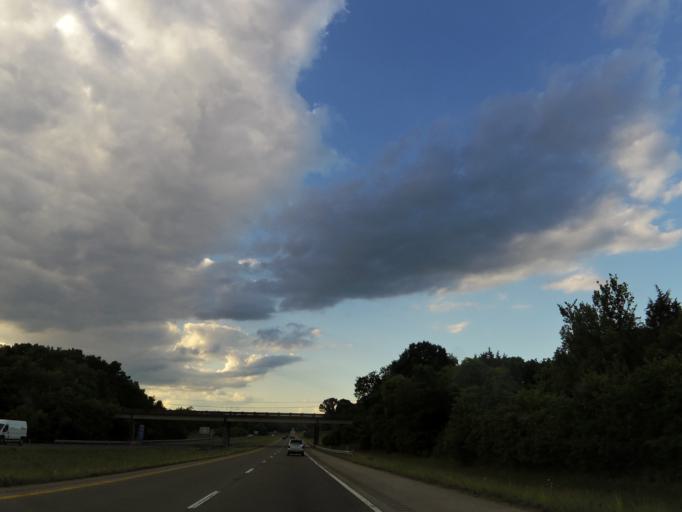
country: US
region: Tennessee
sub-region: Maury County
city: Spring Hill
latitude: 35.6595
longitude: -86.8923
